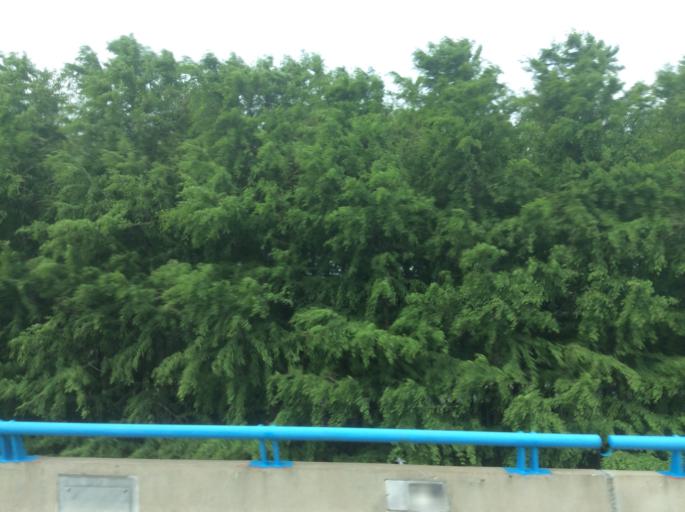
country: CN
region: Shanghai Shi
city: Laogang
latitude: 31.1465
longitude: 121.8024
